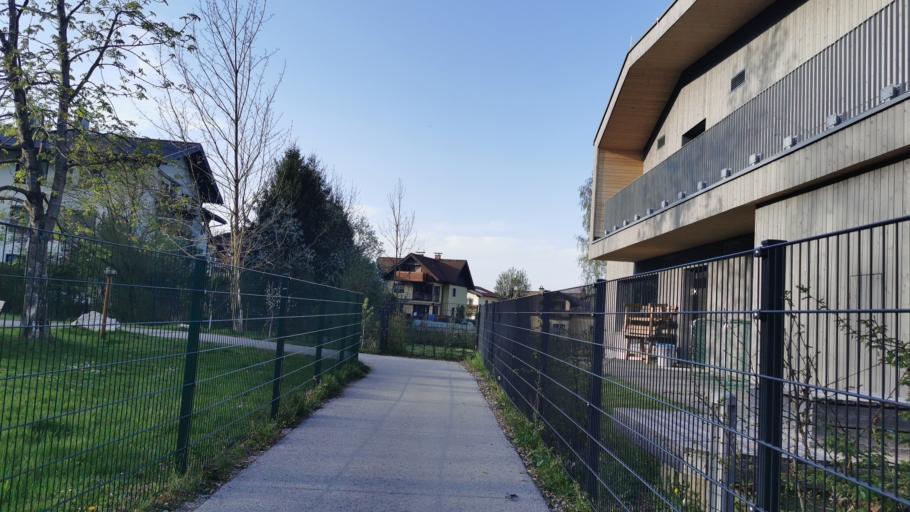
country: AT
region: Salzburg
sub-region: Politischer Bezirk Salzburg-Umgebung
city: Grodig
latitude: 47.7484
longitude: 12.9954
